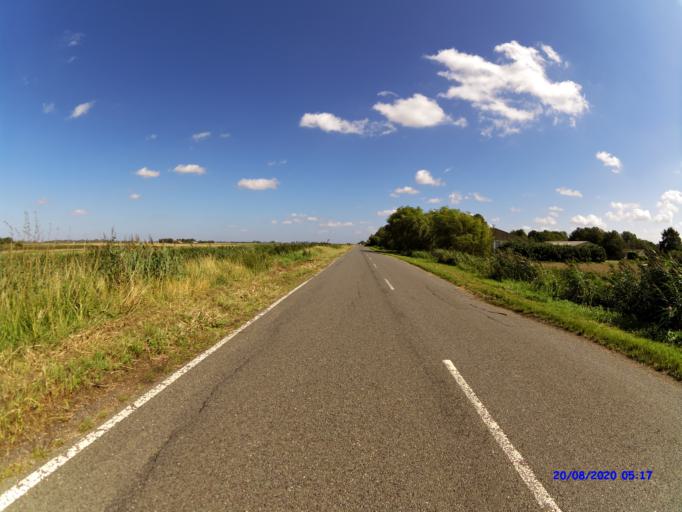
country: GB
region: England
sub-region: Cambridgeshire
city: Whittlesey
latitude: 52.5242
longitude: -0.1128
